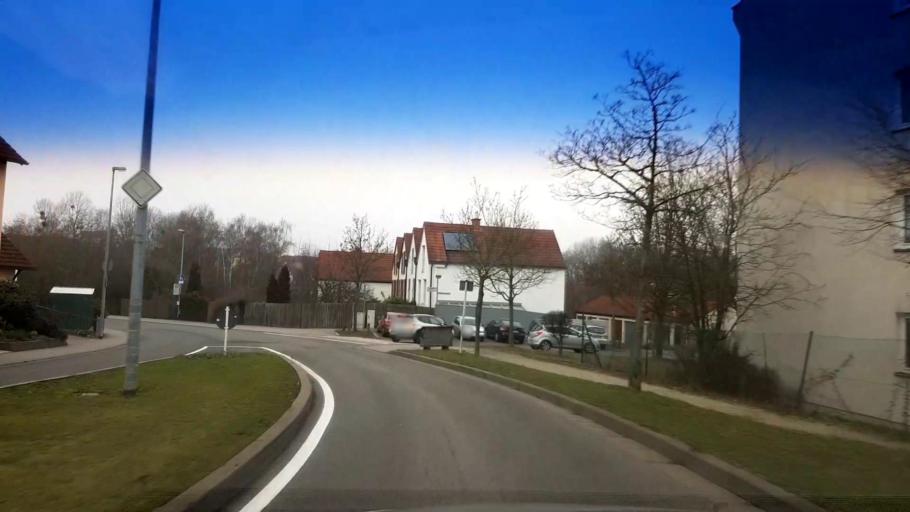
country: DE
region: Bavaria
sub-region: Upper Franconia
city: Hallstadt
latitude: 49.8997
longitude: 10.8660
